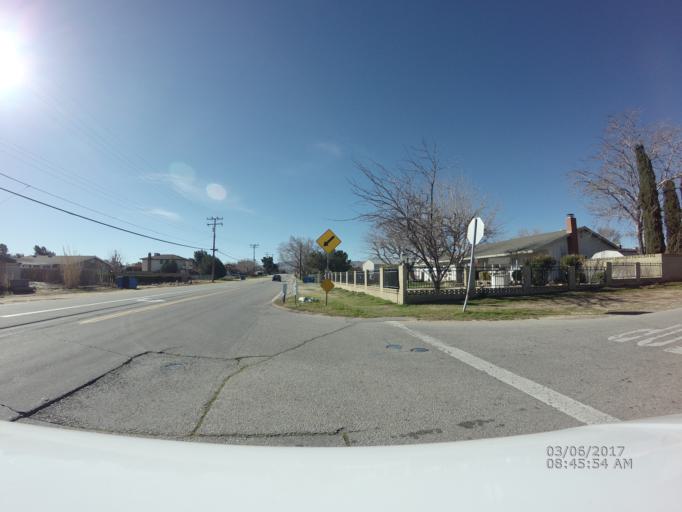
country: US
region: California
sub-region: Los Angeles County
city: Quartz Hill
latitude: 34.6694
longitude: -118.2103
